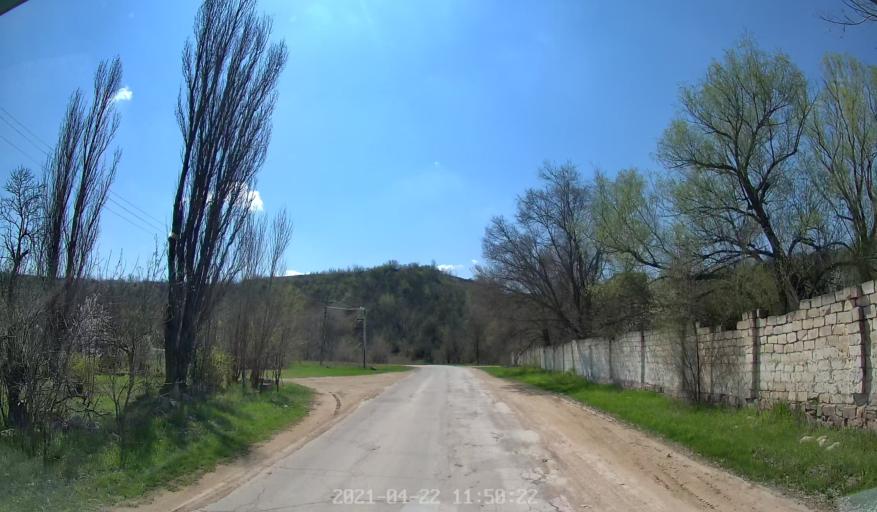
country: MD
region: Chisinau
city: Ciorescu
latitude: 47.1382
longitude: 28.8995
